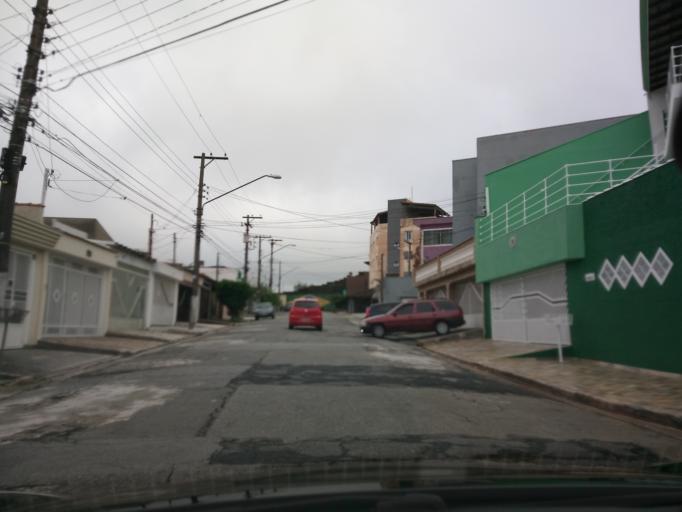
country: BR
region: Sao Paulo
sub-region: Sao Bernardo Do Campo
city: Sao Bernardo do Campo
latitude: -23.7012
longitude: -46.5752
